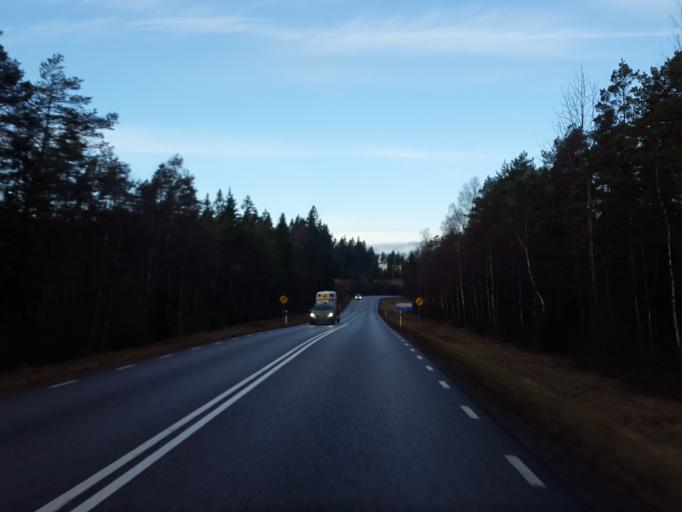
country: SE
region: Vaestra Goetaland
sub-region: Boras Kommun
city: Sandared
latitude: 57.7740
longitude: 12.7978
